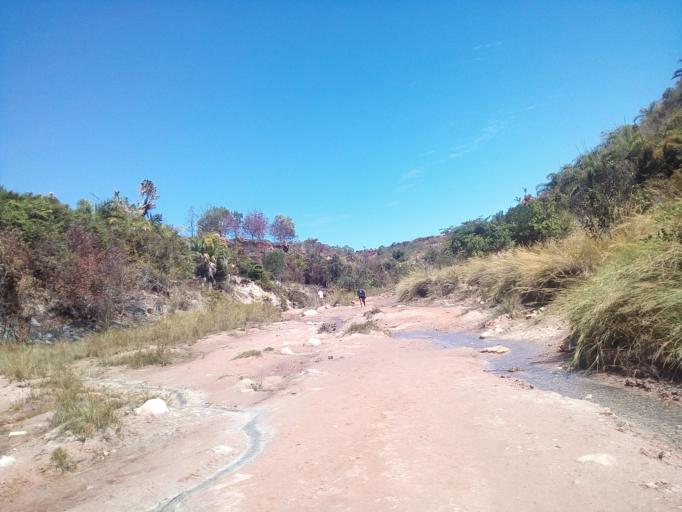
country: MG
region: Boeny
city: Mahajanga
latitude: -15.6322
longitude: 46.3508
